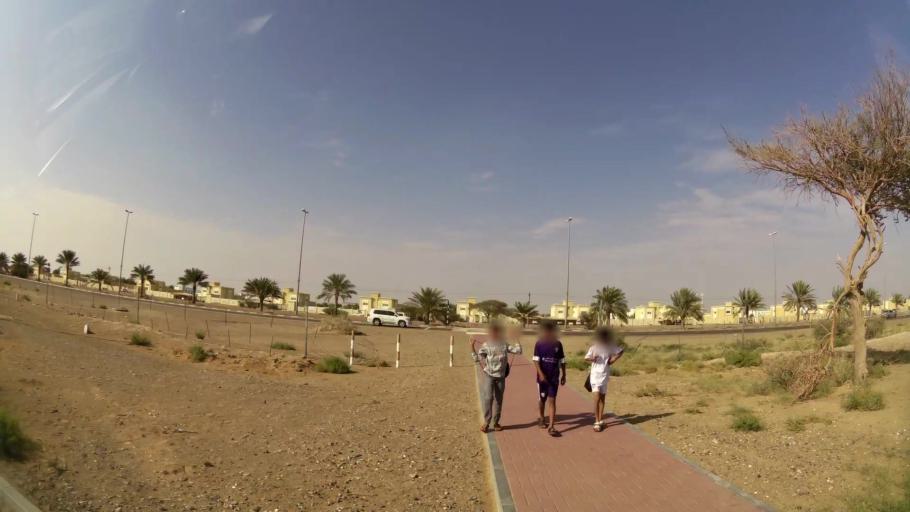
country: AE
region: Abu Dhabi
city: Al Ain
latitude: 24.0926
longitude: 55.8970
